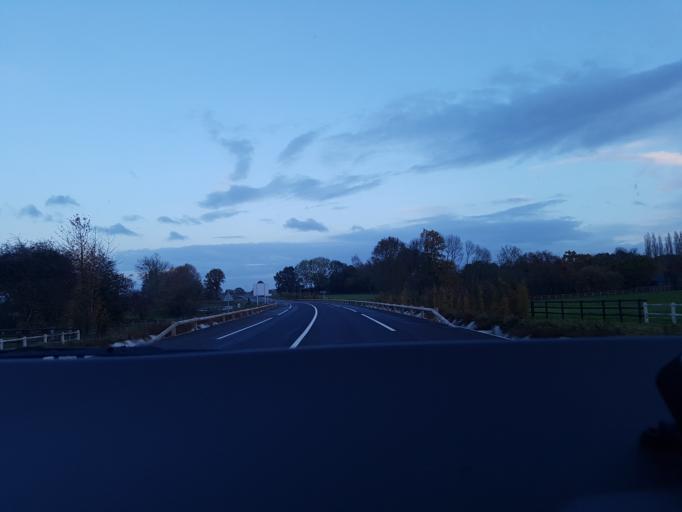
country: FR
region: Haute-Normandie
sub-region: Departement de l'Eure
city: Beuzeville
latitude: 49.3310
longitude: 0.3139
